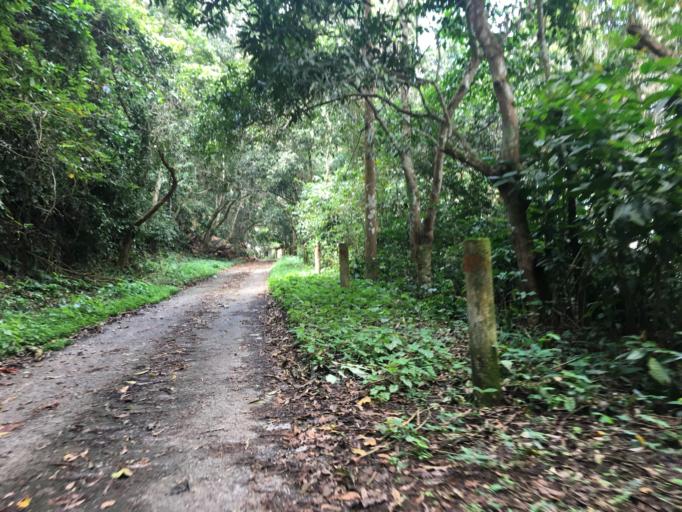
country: TG
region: Plateaux
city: Kpalime
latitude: 6.9532
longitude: 0.5833
